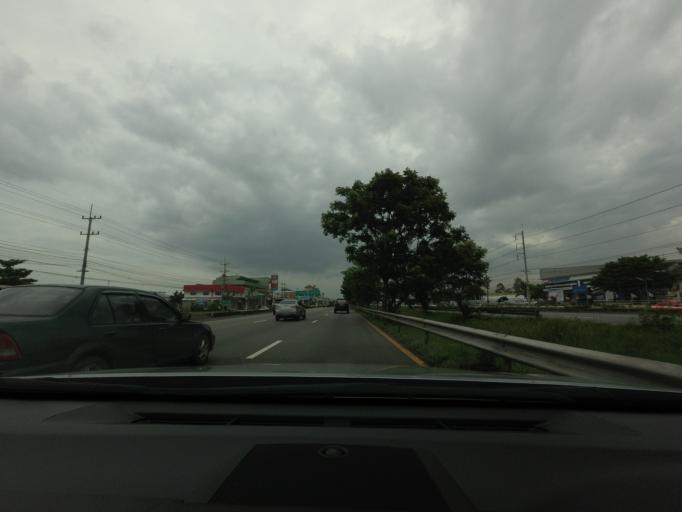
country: TH
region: Samut Sakhon
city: Samut Sakhon
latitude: 13.5783
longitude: 100.3041
